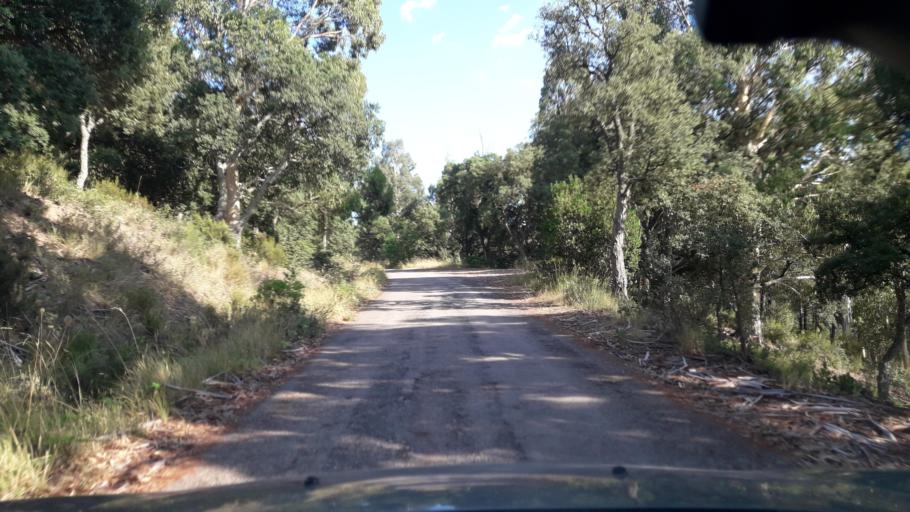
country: FR
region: Provence-Alpes-Cote d'Azur
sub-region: Departement du Var
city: Saint-Raphael
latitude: 43.4994
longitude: 6.7984
